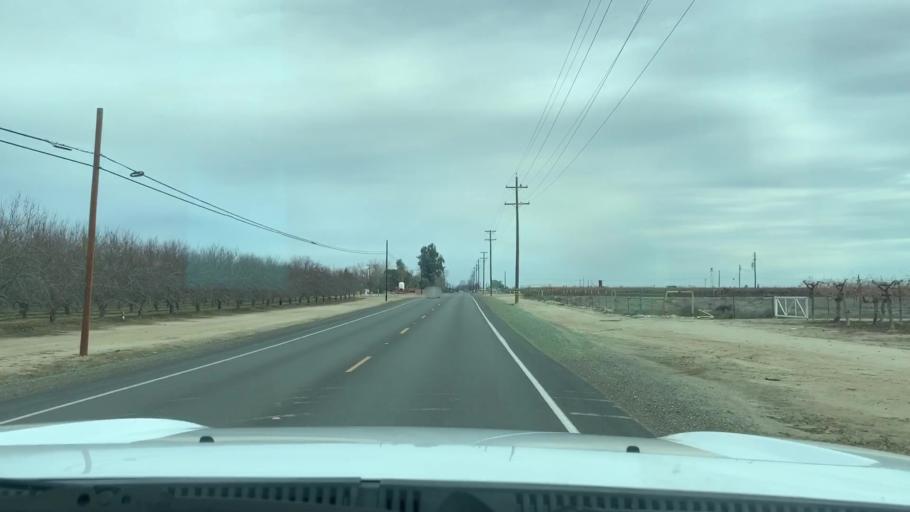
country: US
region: California
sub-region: Kern County
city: Shafter
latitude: 35.4296
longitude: -119.2518
